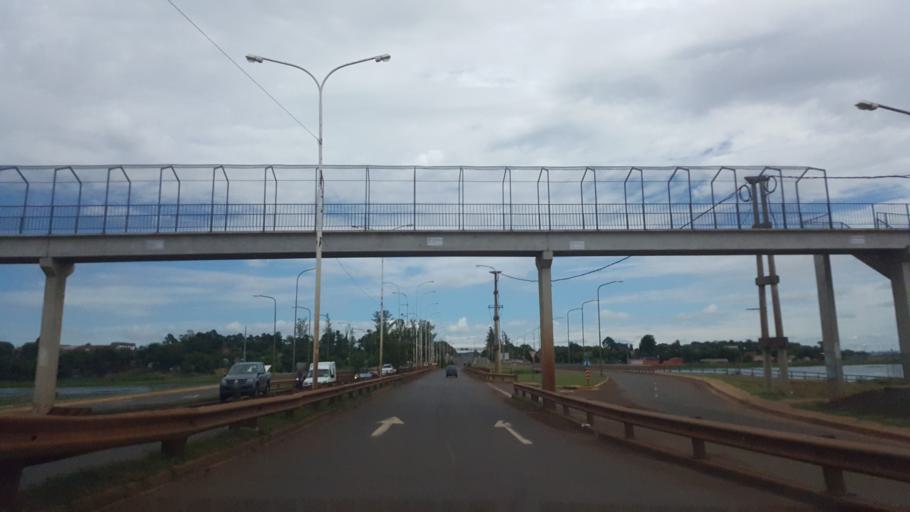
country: AR
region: Misiones
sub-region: Departamento de Capital
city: Posadas
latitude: -27.4217
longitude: -55.8992
